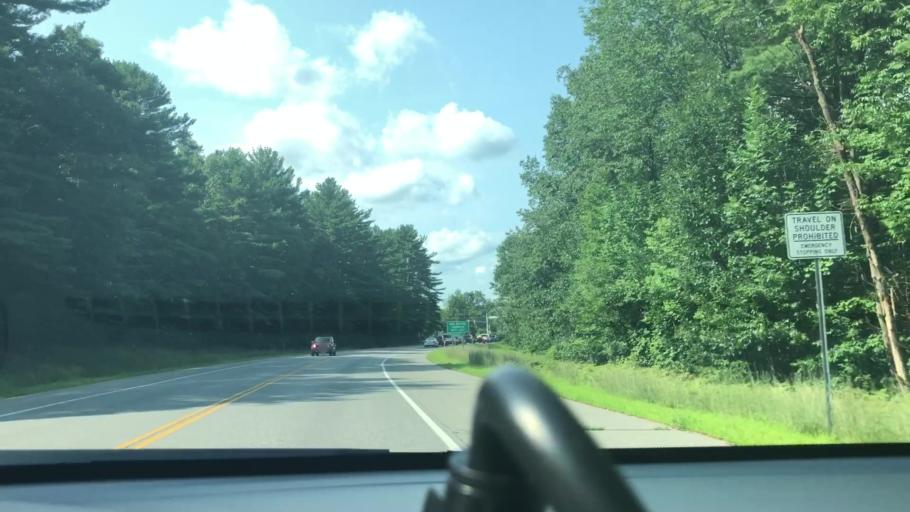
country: US
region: New Hampshire
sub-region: Hillsborough County
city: Pinardville
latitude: 43.0043
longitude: -71.5264
